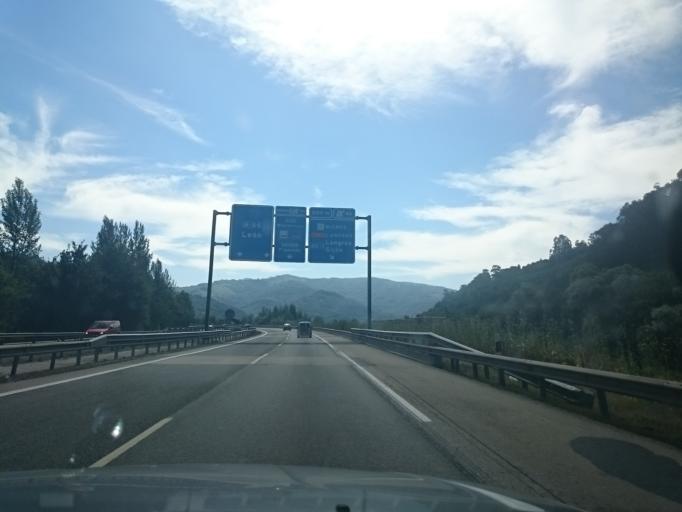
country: ES
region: Asturias
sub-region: Province of Asturias
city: Mieres
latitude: 43.2659
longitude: -5.7960
